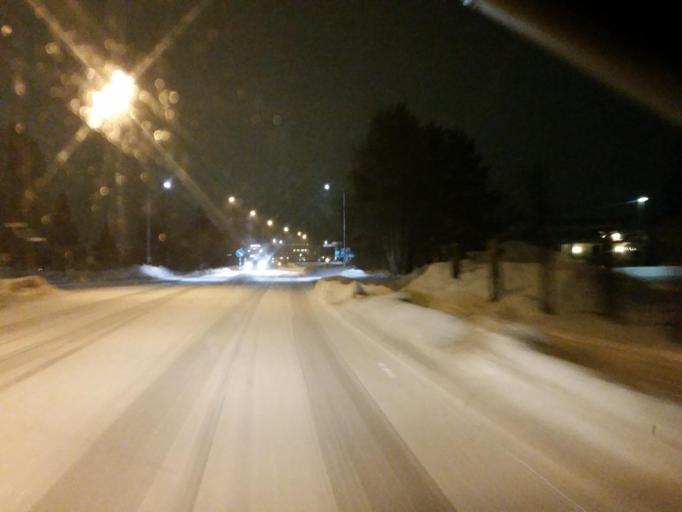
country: SE
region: Norrbotten
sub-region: Alvsbyns Kommun
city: AElvsbyn
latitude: 65.6704
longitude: 20.9992
